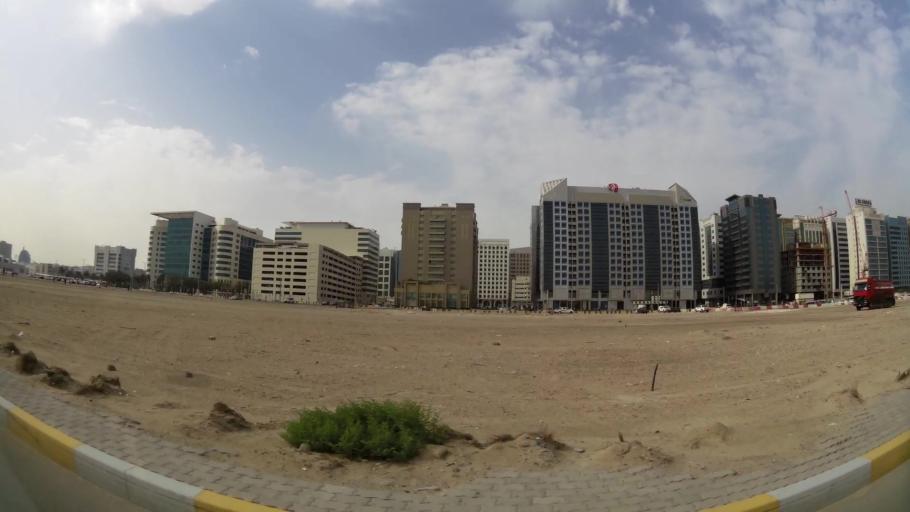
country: AE
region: Abu Dhabi
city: Abu Dhabi
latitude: 24.4661
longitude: 54.3889
